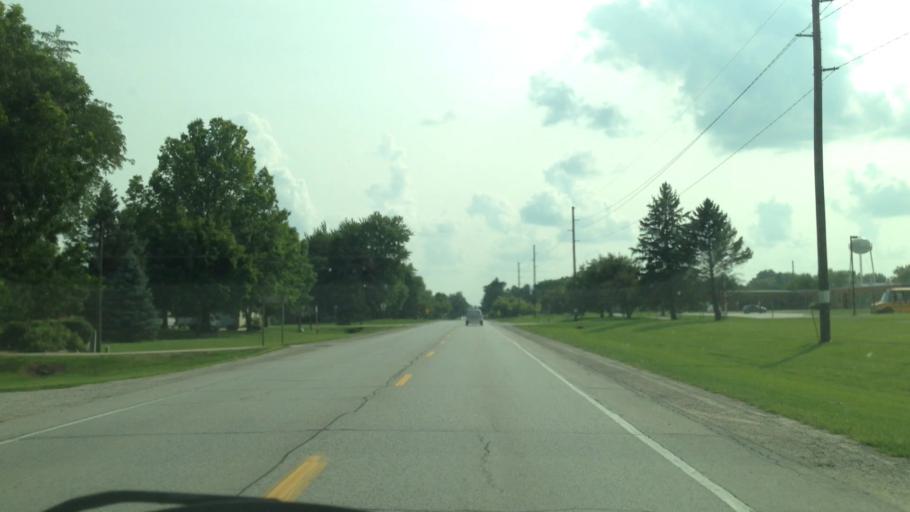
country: US
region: Iowa
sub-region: Benton County
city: Walford
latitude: 41.7987
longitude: -91.8950
